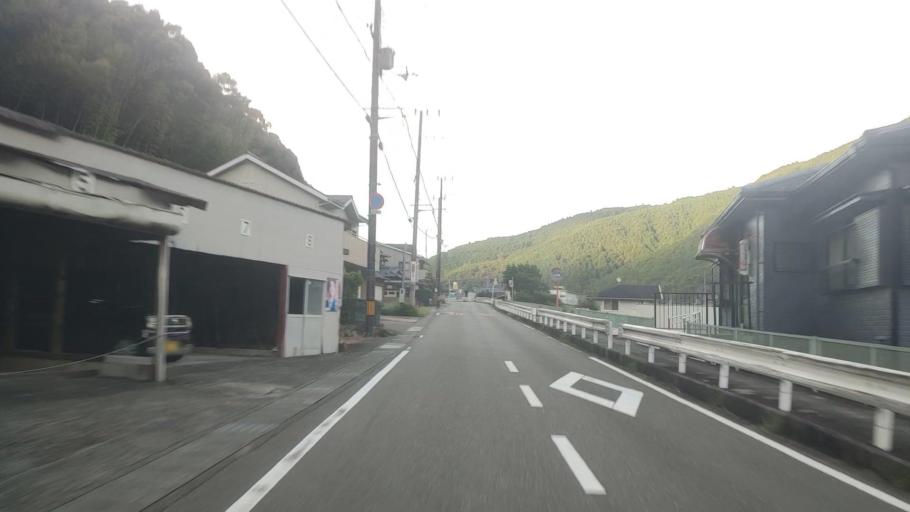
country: JP
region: Wakayama
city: Tanabe
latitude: 33.7896
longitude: 135.5151
